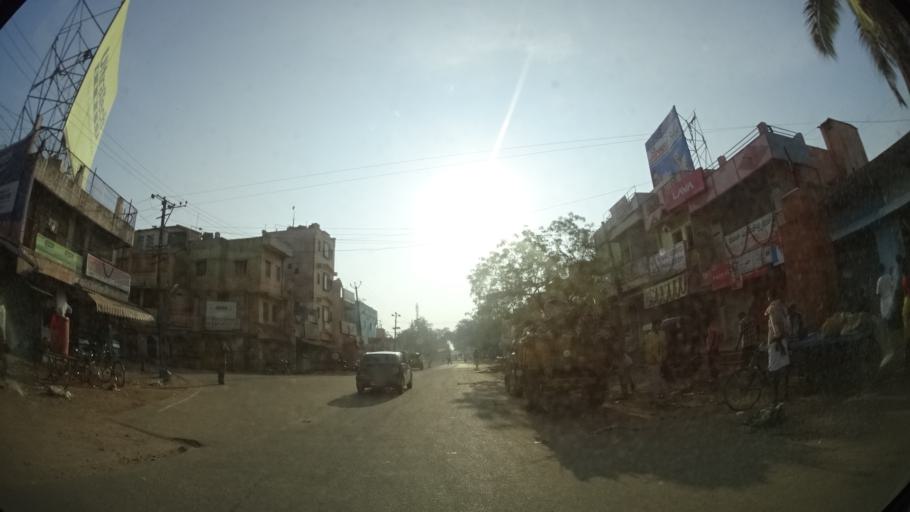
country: IN
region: Karnataka
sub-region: Bellary
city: Hospet
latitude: 15.2664
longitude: 76.3988
